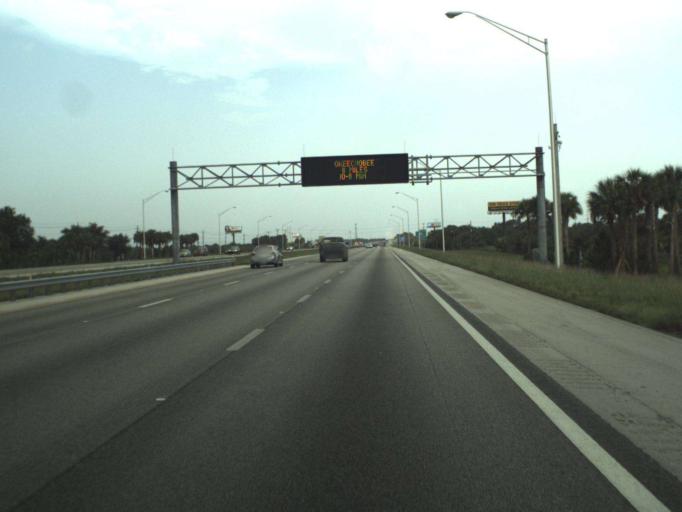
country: US
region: Florida
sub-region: Saint Lucie County
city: Lakewood Park
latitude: 27.5407
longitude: -80.4665
